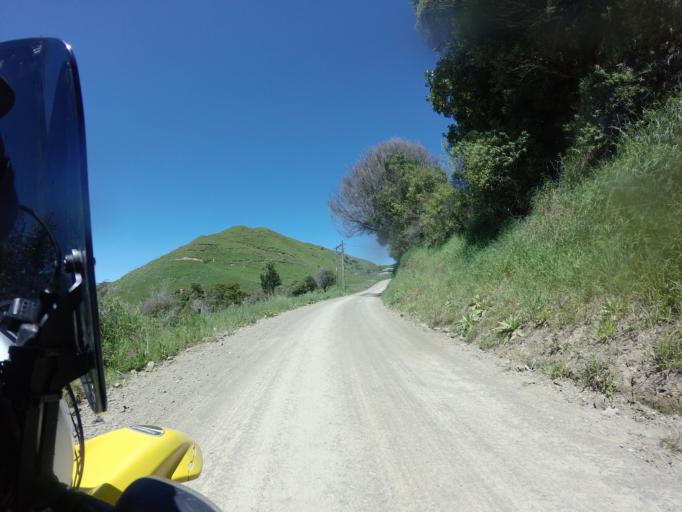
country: NZ
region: Bay of Plenty
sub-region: Opotiki District
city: Opotiki
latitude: -38.3962
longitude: 177.4596
